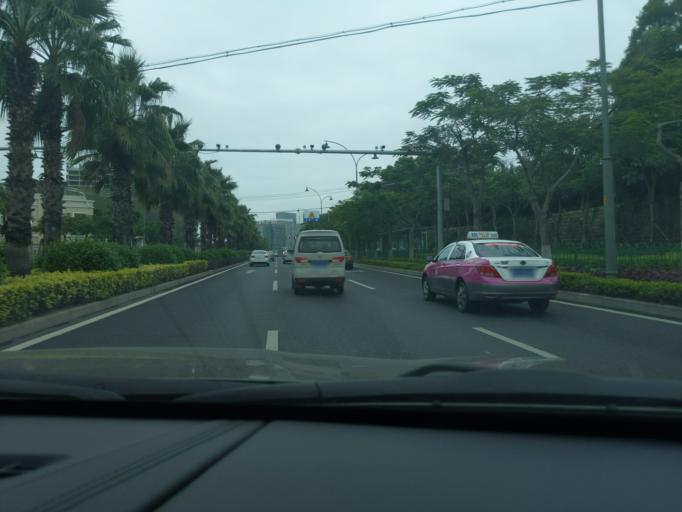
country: CN
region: Fujian
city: Liuwudian
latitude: 24.4984
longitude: 118.1710
